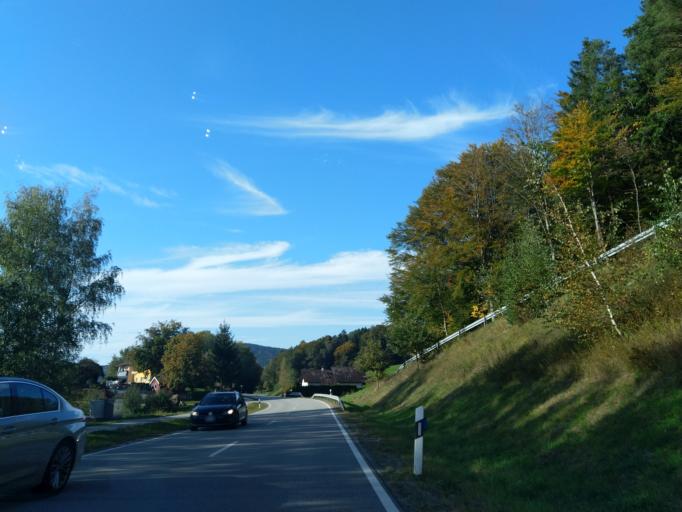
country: DE
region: Bavaria
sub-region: Lower Bavaria
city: Bernried
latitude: 48.9054
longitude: 12.8910
